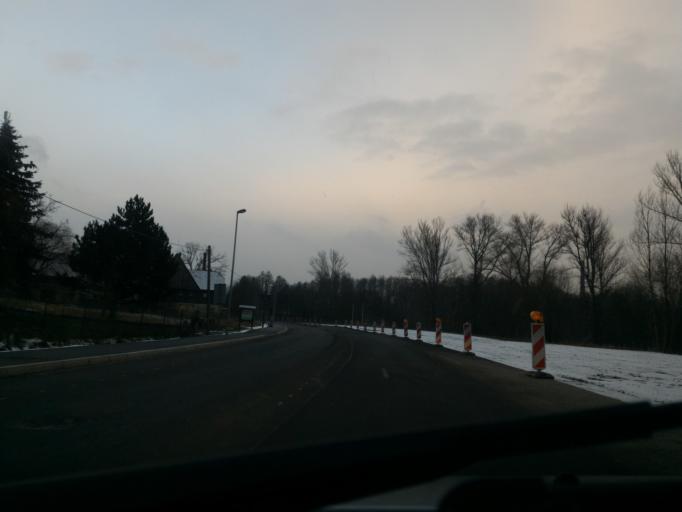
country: DE
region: Saxony
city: Seifhennersdorf
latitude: 50.9234
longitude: 14.6073
